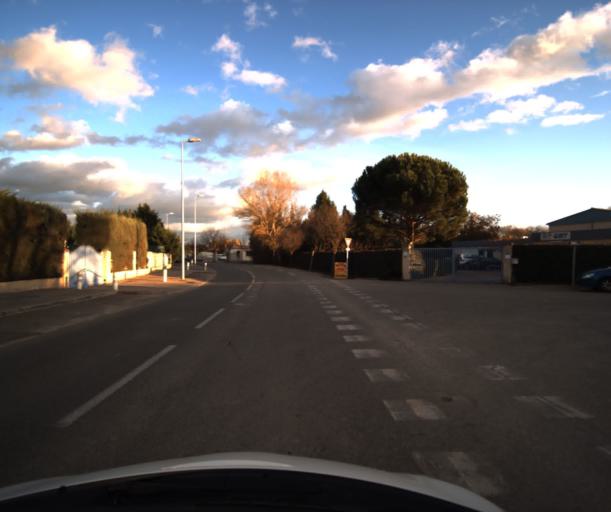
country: FR
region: Provence-Alpes-Cote d'Azur
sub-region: Departement du Vaucluse
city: Pertuis
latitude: 43.6743
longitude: 5.5019
